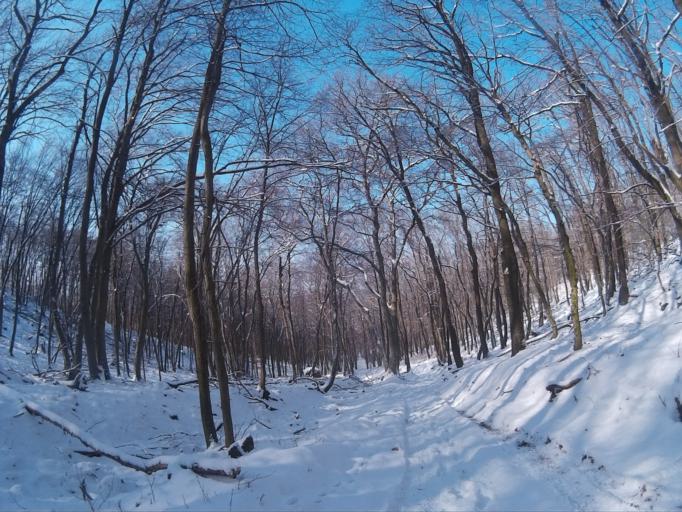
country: HU
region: Komarom-Esztergom
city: Labatlan
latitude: 47.7066
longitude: 18.5059
